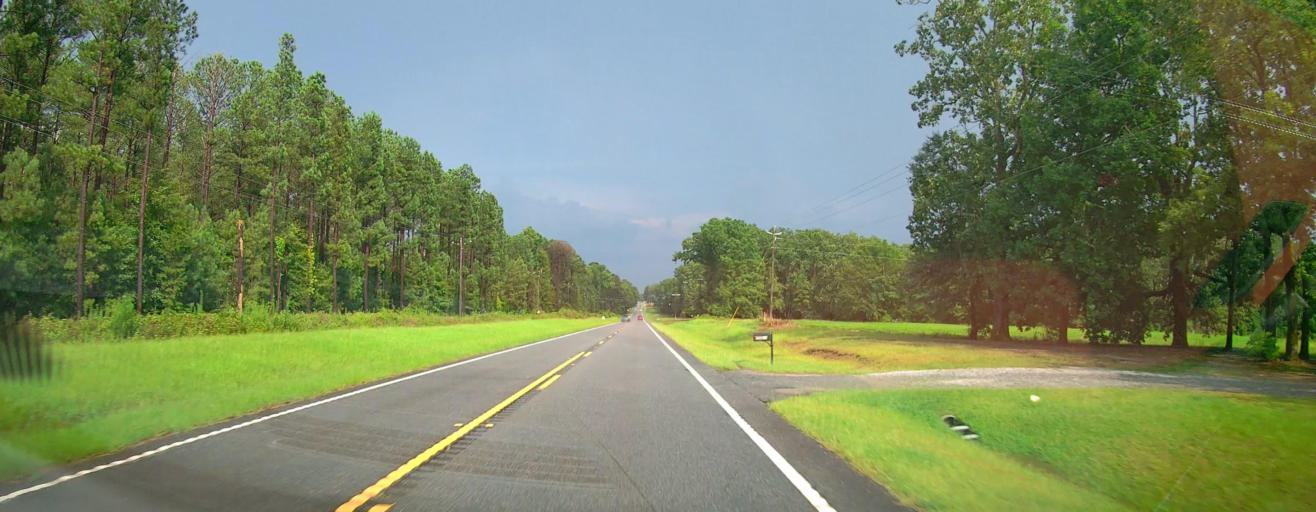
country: US
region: Georgia
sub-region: Twiggs County
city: Jeffersonville
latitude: 32.6072
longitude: -83.2626
